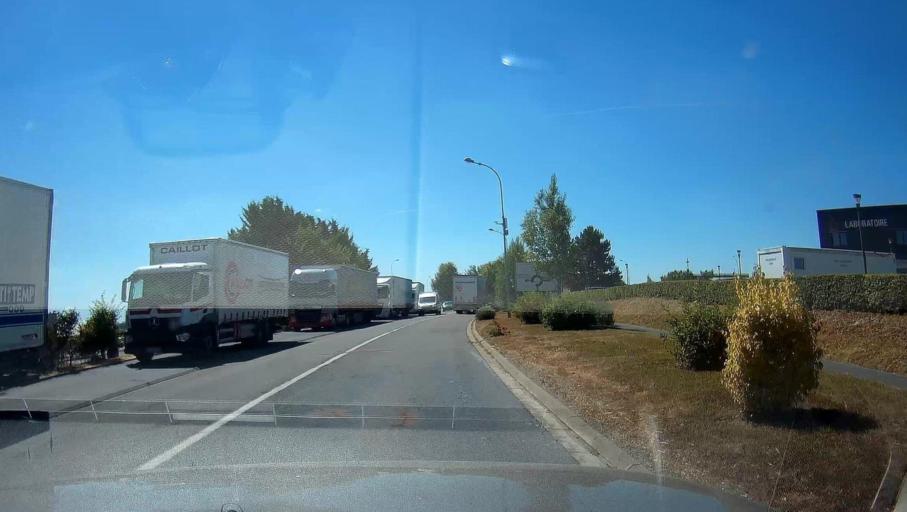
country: FR
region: Champagne-Ardenne
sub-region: Departement des Ardennes
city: Rethel
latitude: 49.5224
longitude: 4.3714
